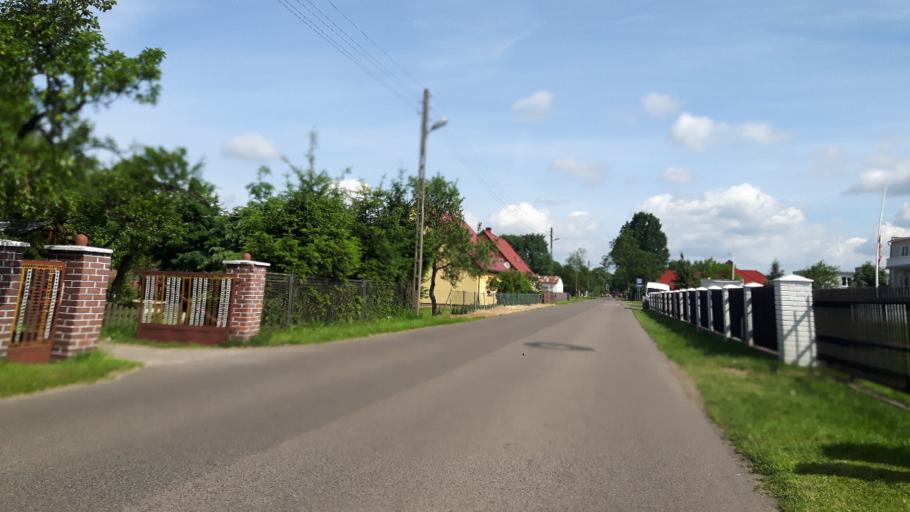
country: PL
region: West Pomeranian Voivodeship
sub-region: Powiat goleniowski
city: Goleniow
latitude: 53.4750
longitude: 14.7741
